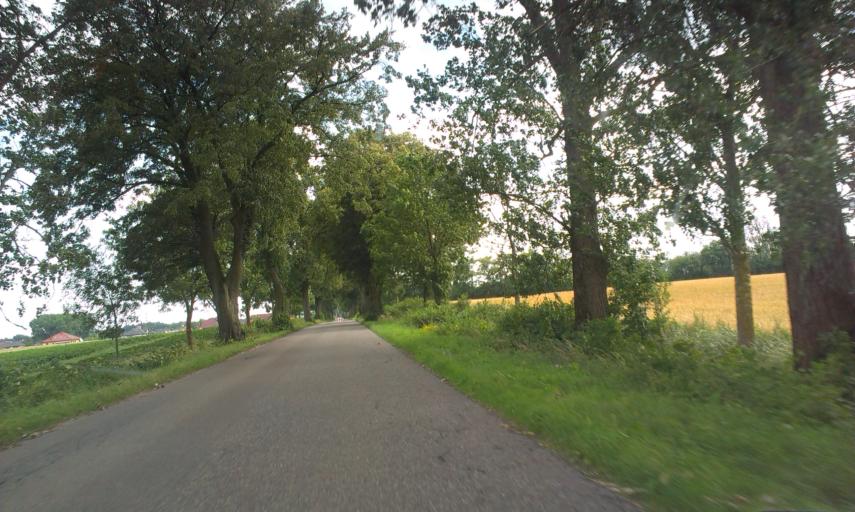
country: PL
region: Greater Poland Voivodeship
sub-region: Powiat zlotowski
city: Zlotow
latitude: 53.3803
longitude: 17.0187
